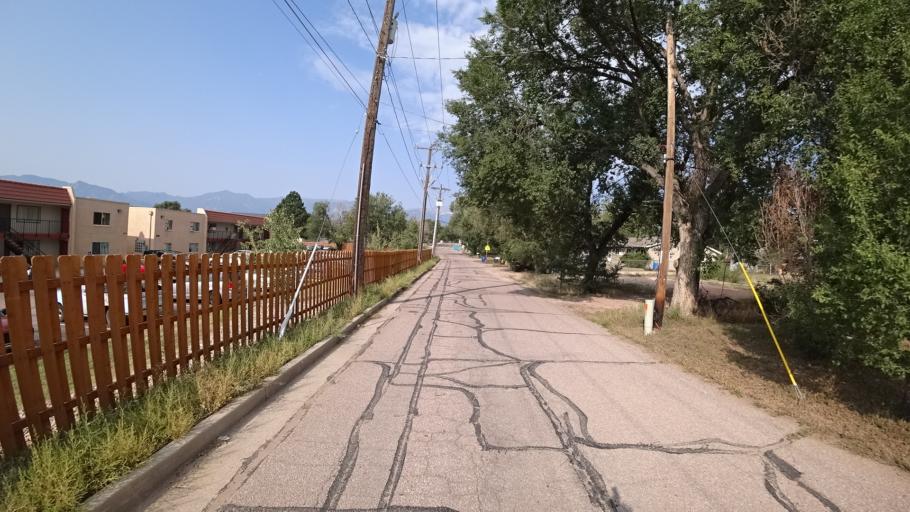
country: US
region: Colorado
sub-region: El Paso County
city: Colorado Springs
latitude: 38.8471
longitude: -104.7815
